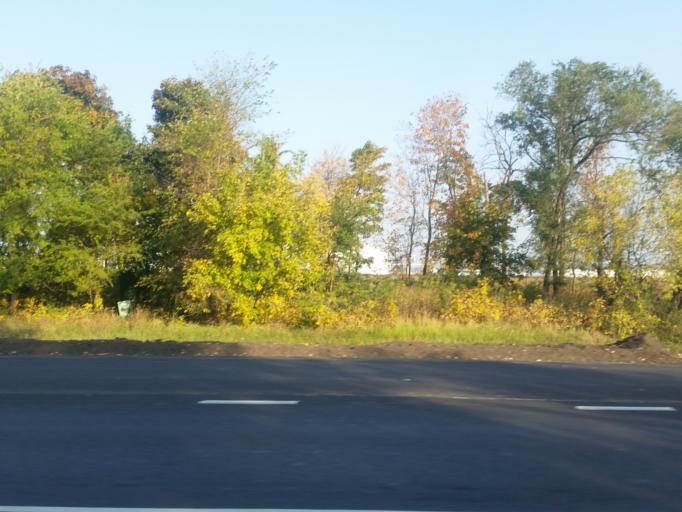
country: RU
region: Ulyanovsk
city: Mirnyy
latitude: 54.3630
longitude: 48.6944
